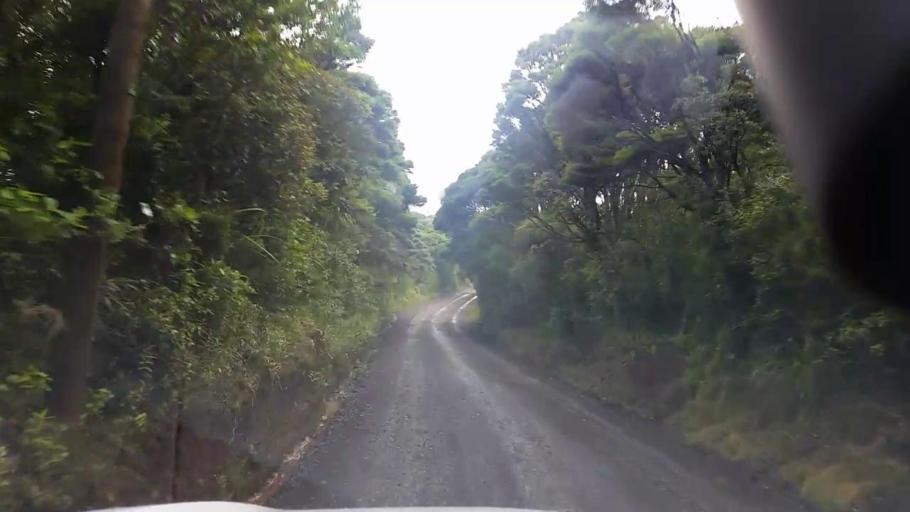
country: NZ
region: Auckland
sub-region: Auckland
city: Muriwai Beach
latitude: -36.9273
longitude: 174.4857
